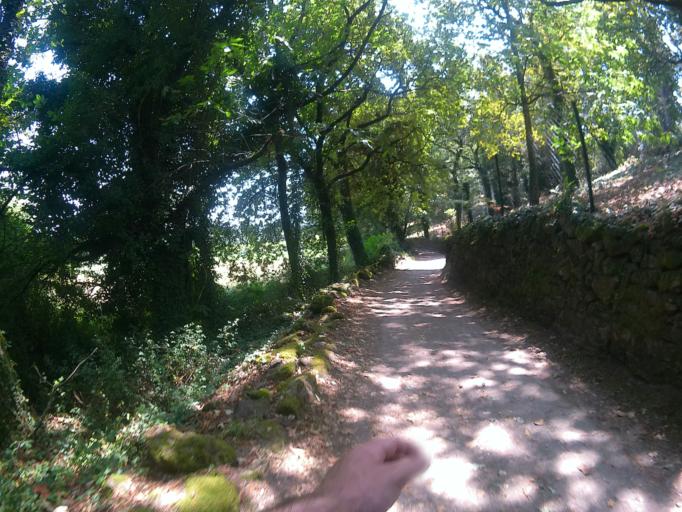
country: PT
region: Viana do Castelo
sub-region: Ponte de Lima
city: Ponte de Lima
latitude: 41.7750
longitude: -8.5693
